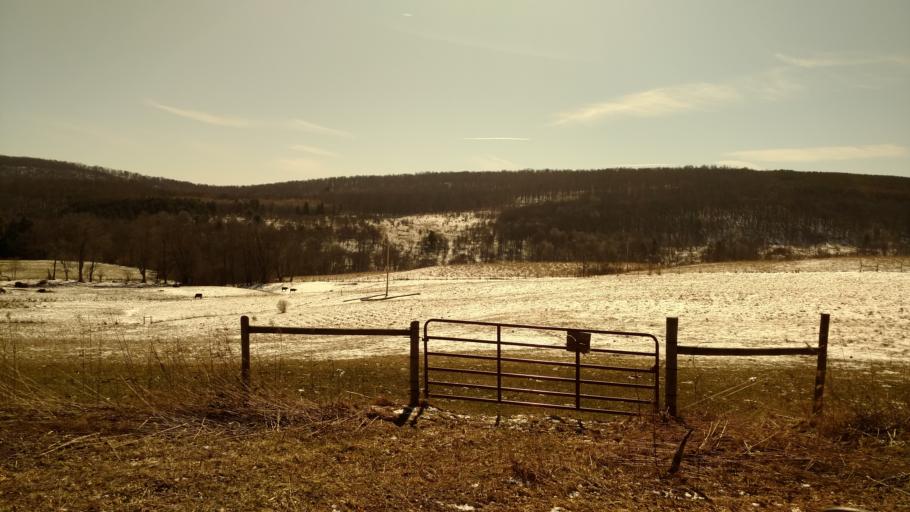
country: US
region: New York
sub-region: Allegany County
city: Wellsville
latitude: 42.0726
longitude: -78.0091
